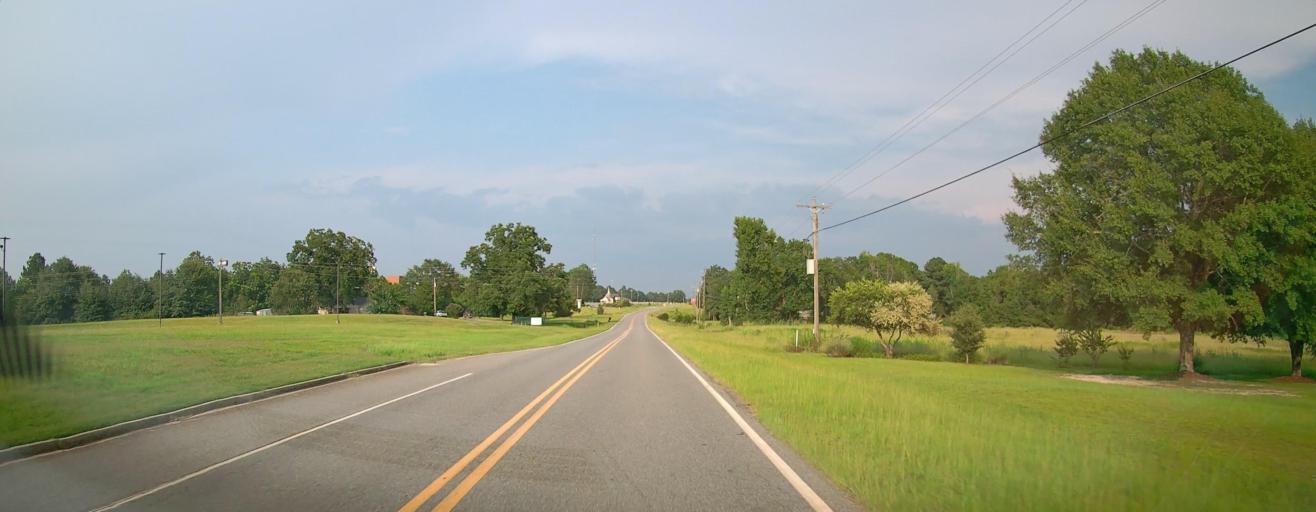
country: US
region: Georgia
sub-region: Laurens County
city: Dublin
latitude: 32.4843
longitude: -82.9433
